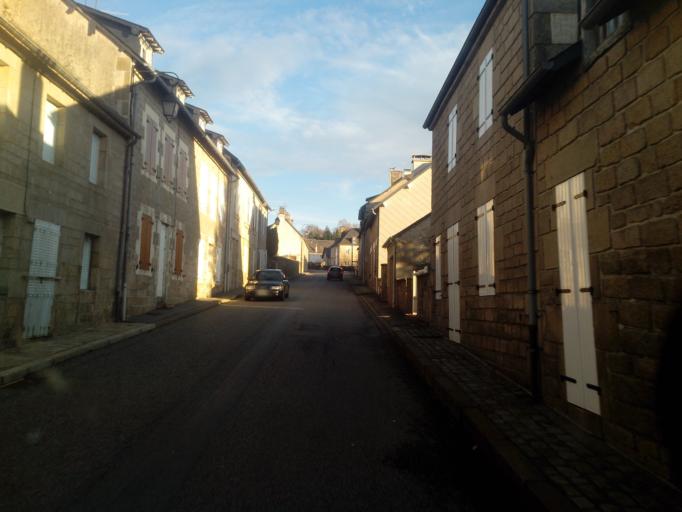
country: FR
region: Limousin
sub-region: Departement de la Correze
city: Bugeat
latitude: 45.5969
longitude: 1.9297
